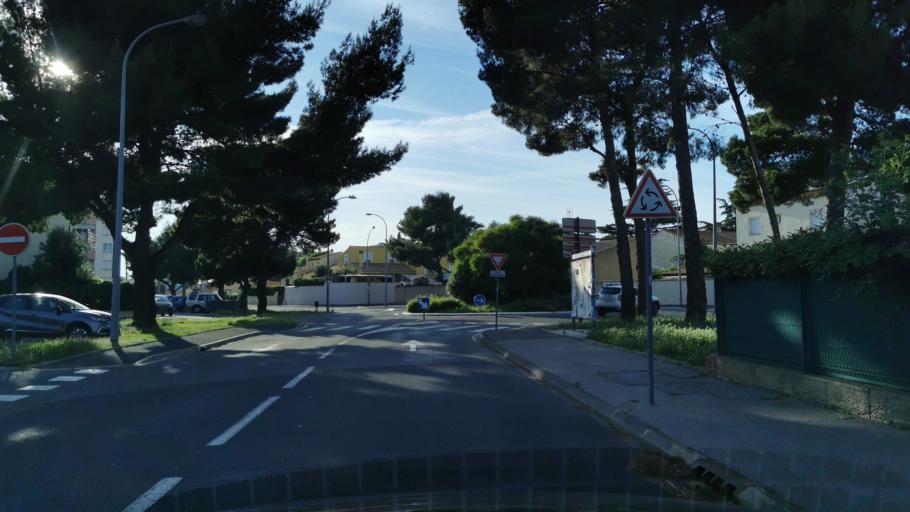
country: FR
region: Languedoc-Roussillon
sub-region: Departement de l'Aude
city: Narbonne
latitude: 43.1857
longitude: 3.0209
